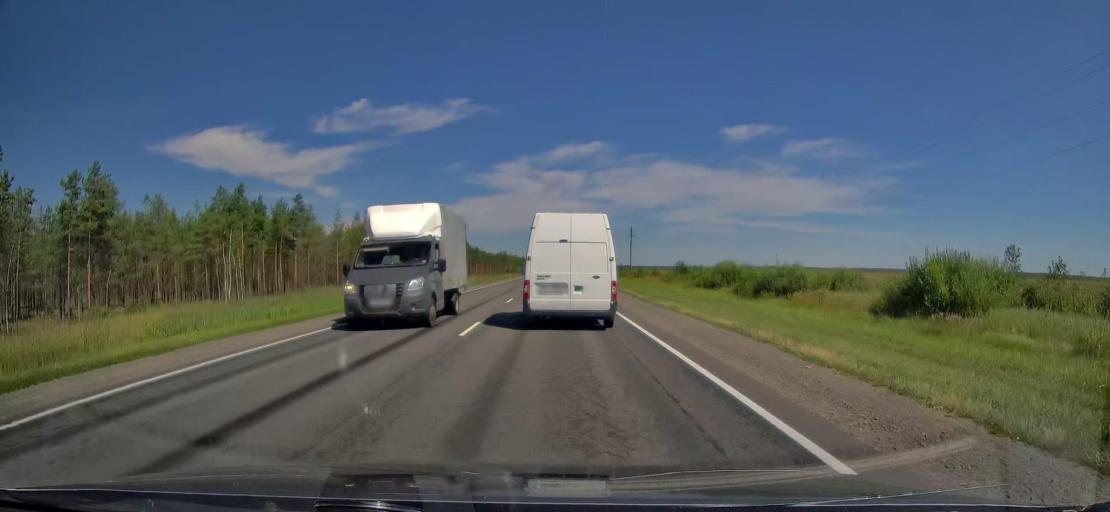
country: RU
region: Vologda
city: Khokhlovo
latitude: 58.9801
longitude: 37.3269
